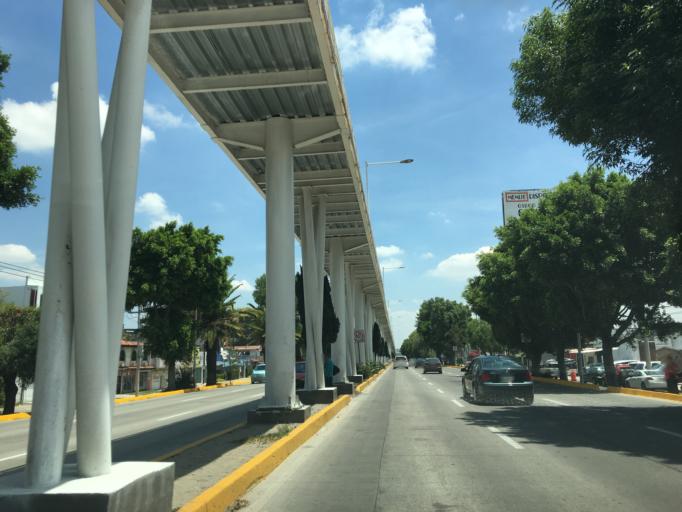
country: MX
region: Puebla
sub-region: Cuautlancingo
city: Sanctorum
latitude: 19.0846
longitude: -98.2288
